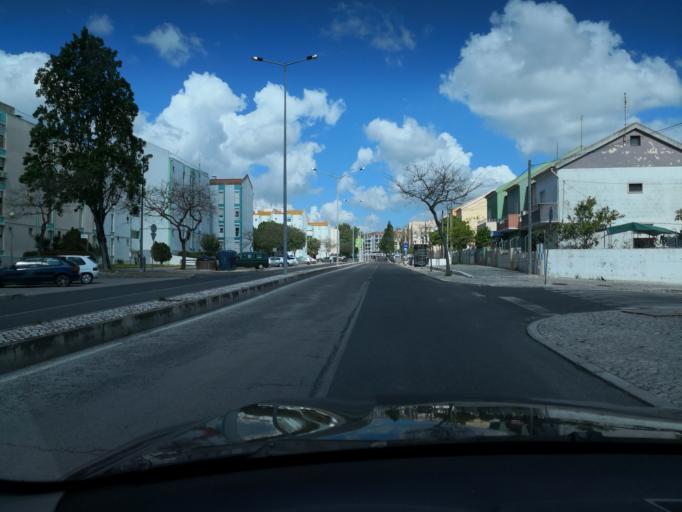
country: PT
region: Setubal
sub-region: Setubal
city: Setubal
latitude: 38.5241
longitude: -8.8637
